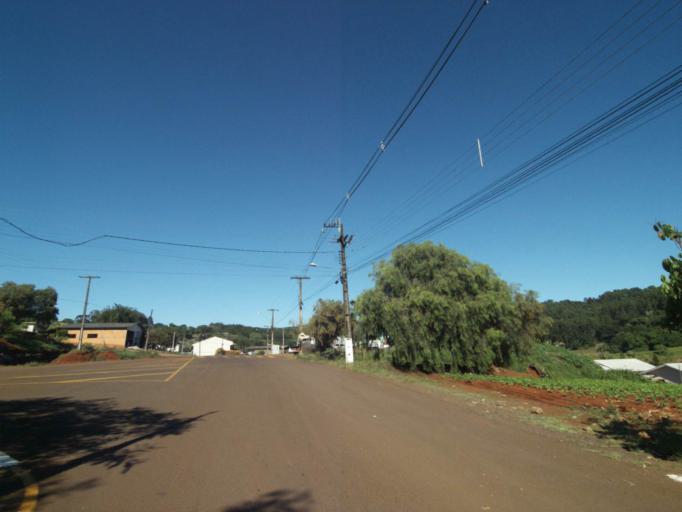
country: BR
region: Santa Catarina
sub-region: Sao Lourenco Do Oeste
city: Sao Lourenco dOeste
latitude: -26.2670
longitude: -52.7853
